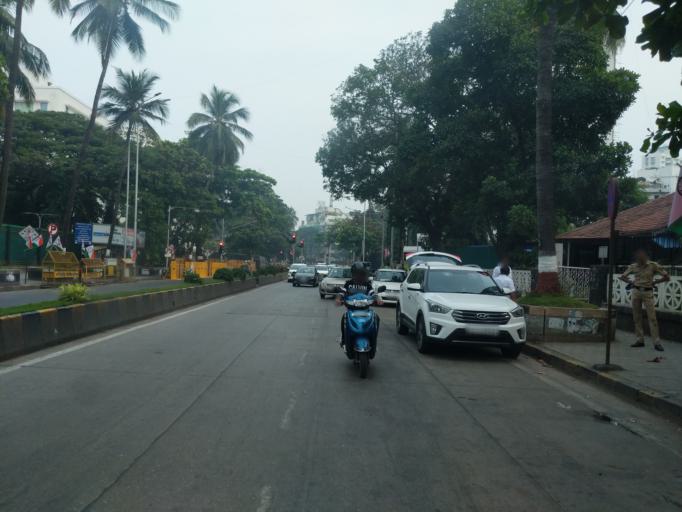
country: IN
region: Maharashtra
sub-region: Raigarh
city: Uran
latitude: 18.9274
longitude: 72.8255
